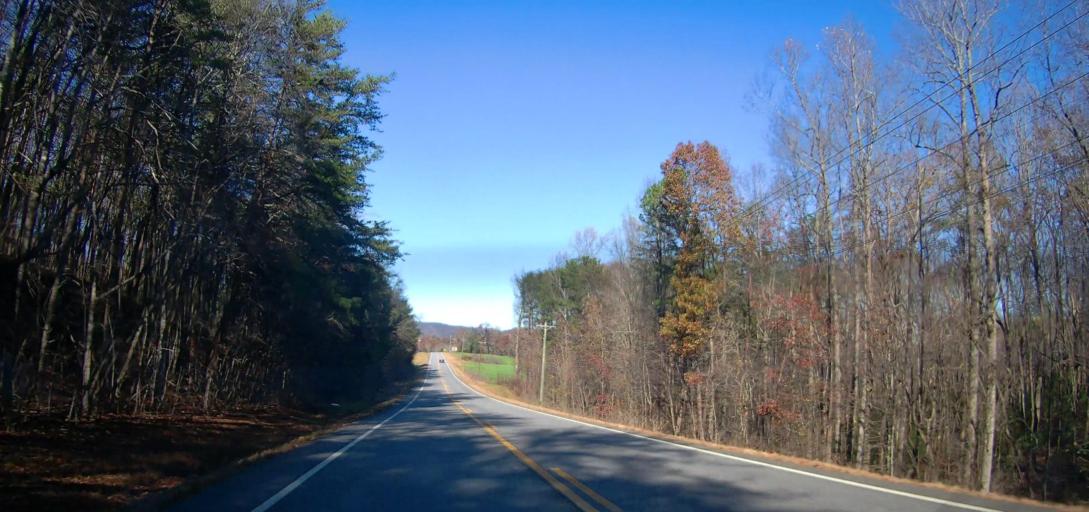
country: US
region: Georgia
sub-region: White County
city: Cleveland
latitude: 34.6481
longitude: -83.7972
